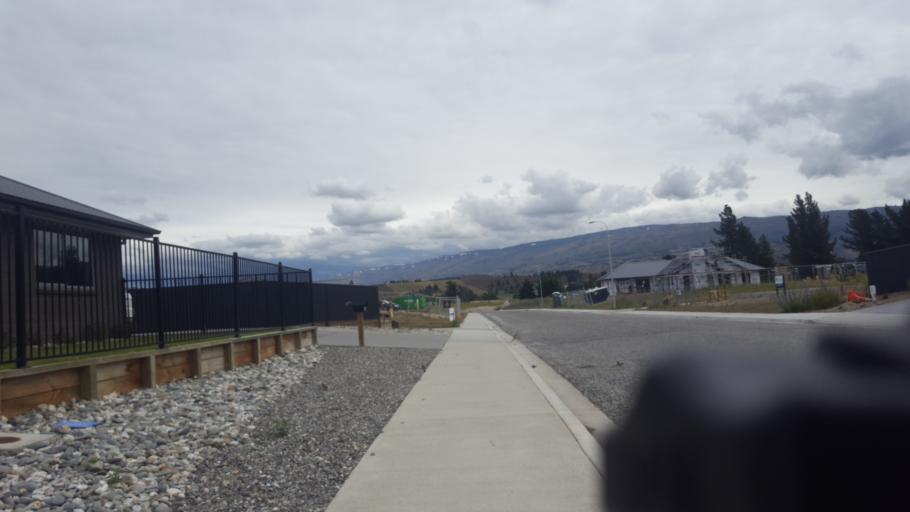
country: NZ
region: Otago
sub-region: Queenstown-Lakes District
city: Wanaka
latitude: -45.2440
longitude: 169.3737
